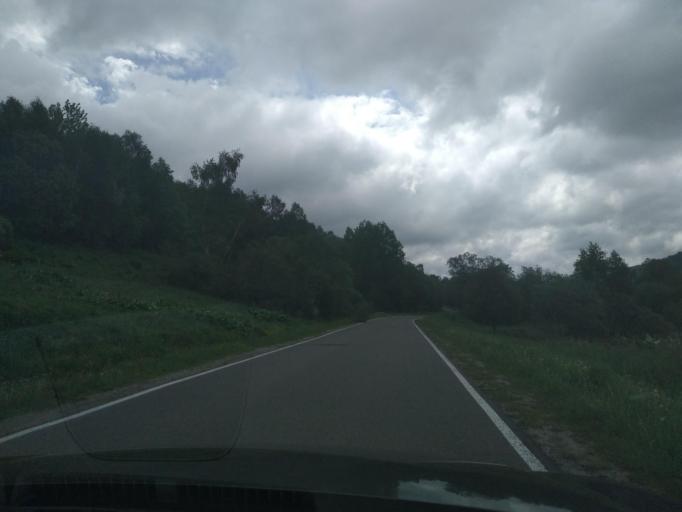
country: PL
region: Subcarpathian Voivodeship
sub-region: Powiat bieszczadzki
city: Lutowiska
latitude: 49.0727
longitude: 22.6747
